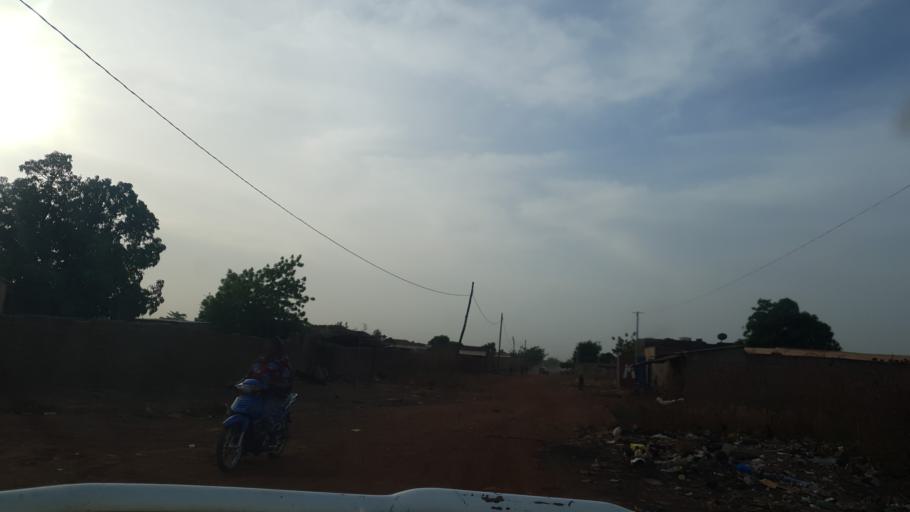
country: ML
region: Segou
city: Baroueli
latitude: 12.7849
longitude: -6.9455
